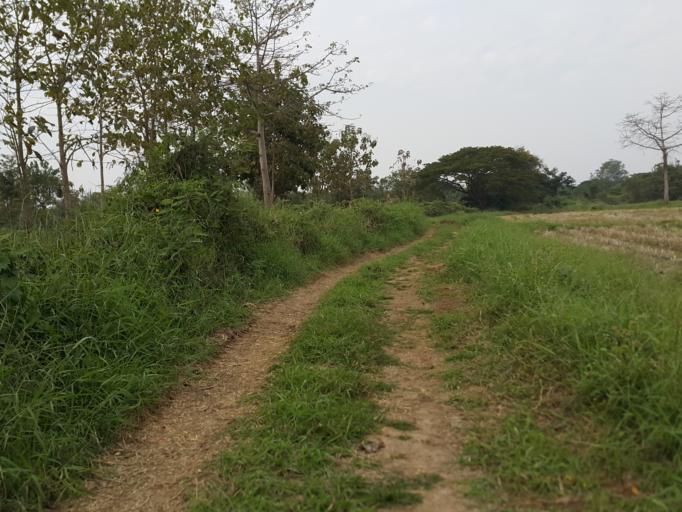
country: TH
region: Chiang Mai
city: San Kamphaeng
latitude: 18.7995
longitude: 99.1159
